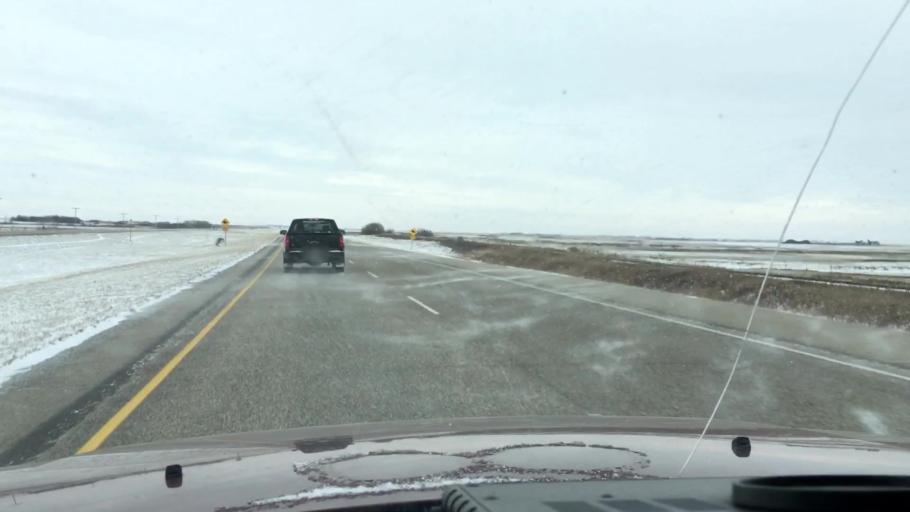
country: CA
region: Saskatchewan
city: Saskatoon
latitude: 51.6056
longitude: -106.4057
